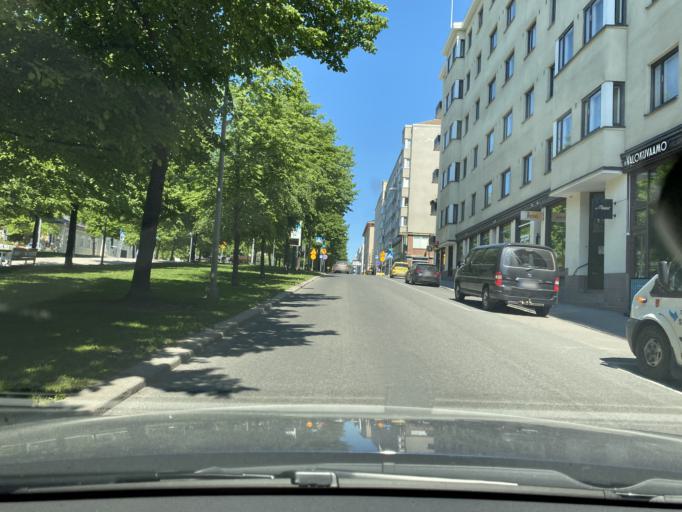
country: FI
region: Pirkanmaa
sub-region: Tampere
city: Tampere
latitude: 61.4956
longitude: 23.7530
